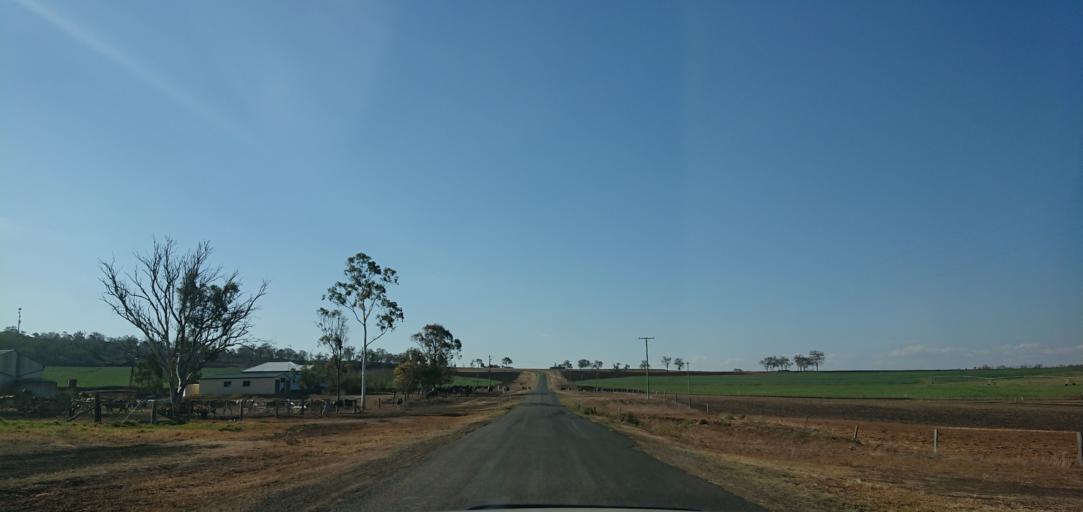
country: AU
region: Queensland
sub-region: Toowoomba
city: Westbrook
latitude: -27.7082
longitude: 151.7162
